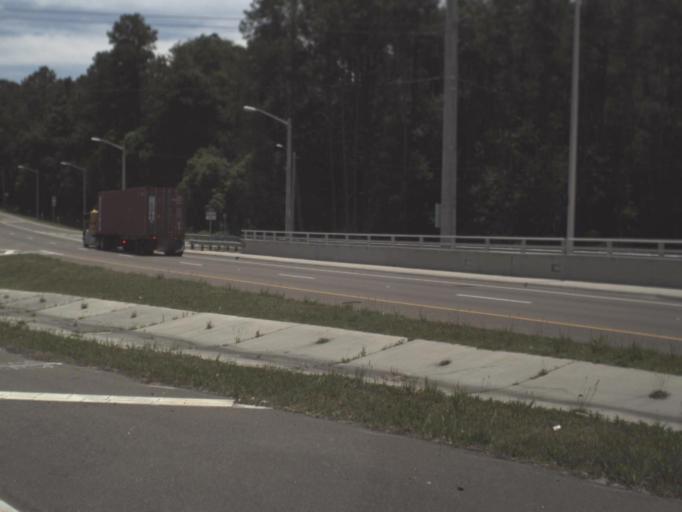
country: US
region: Florida
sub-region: Duval County
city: Jacksonville
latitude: 30.3597
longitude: -81.7131
